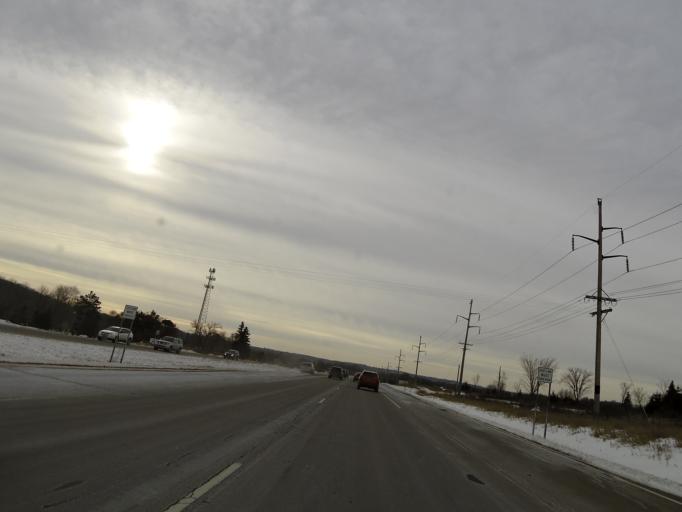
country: US
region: Minnesota
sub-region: Carver County
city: Carver
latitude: 44.7414
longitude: -93.5879
